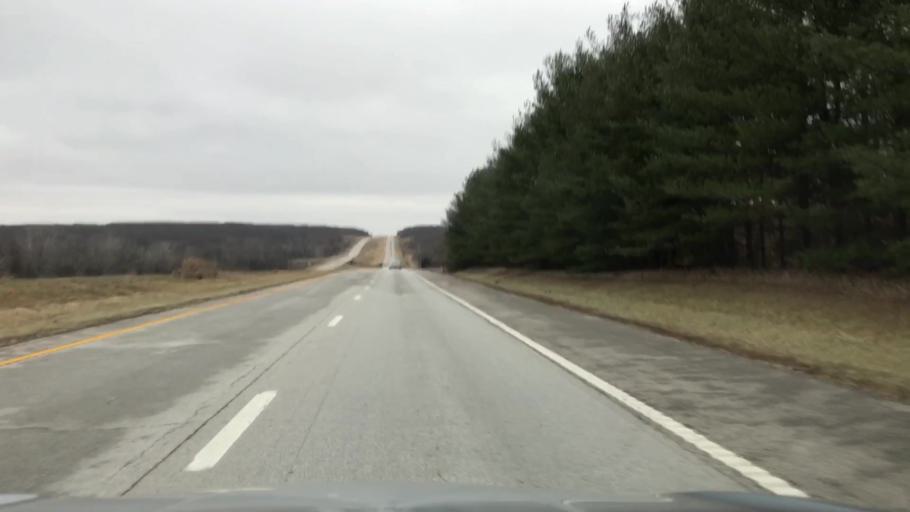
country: US
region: Missouri
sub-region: Linn County
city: Marceline
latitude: 39.7590
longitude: -92.8635
